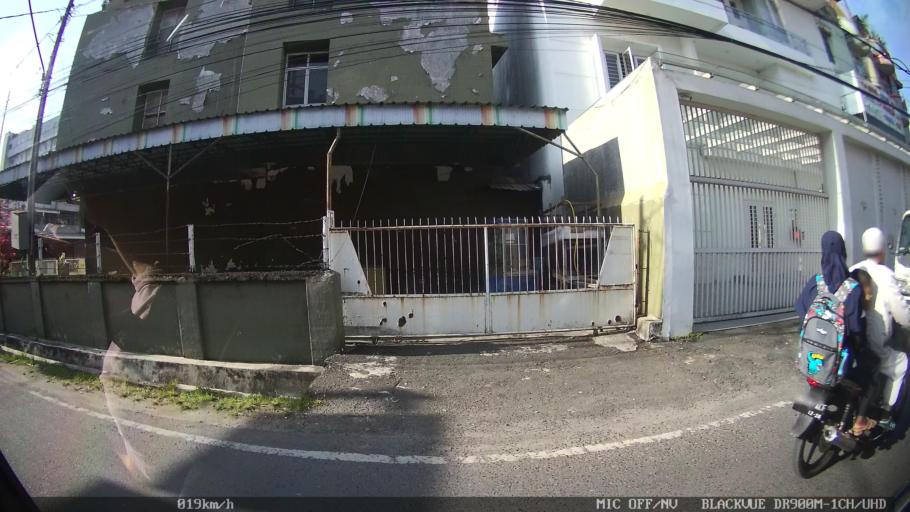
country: ID
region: North Sumatra
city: Medan
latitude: 3.5948
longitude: 98.6673
